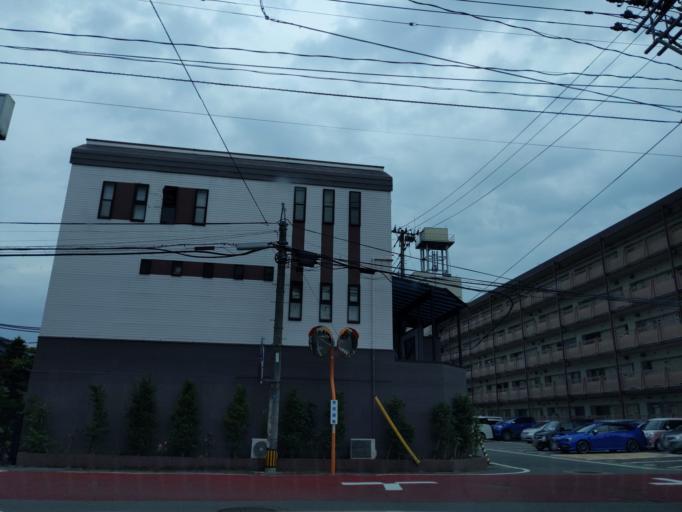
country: JP
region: Fukushima
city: Koriyama
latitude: 37.3837
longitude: 140.3566
